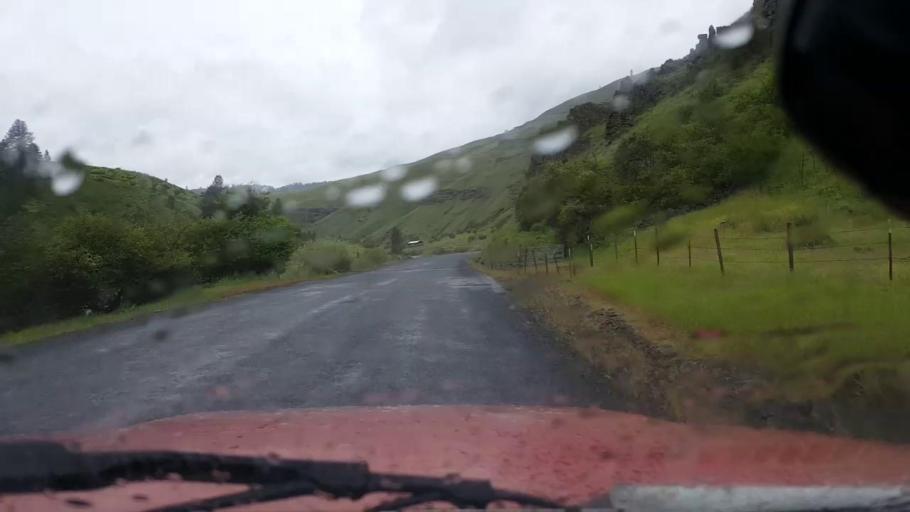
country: US
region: Washington
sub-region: Asotin County
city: Asotin
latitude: 46.0263
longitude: -117.3257
